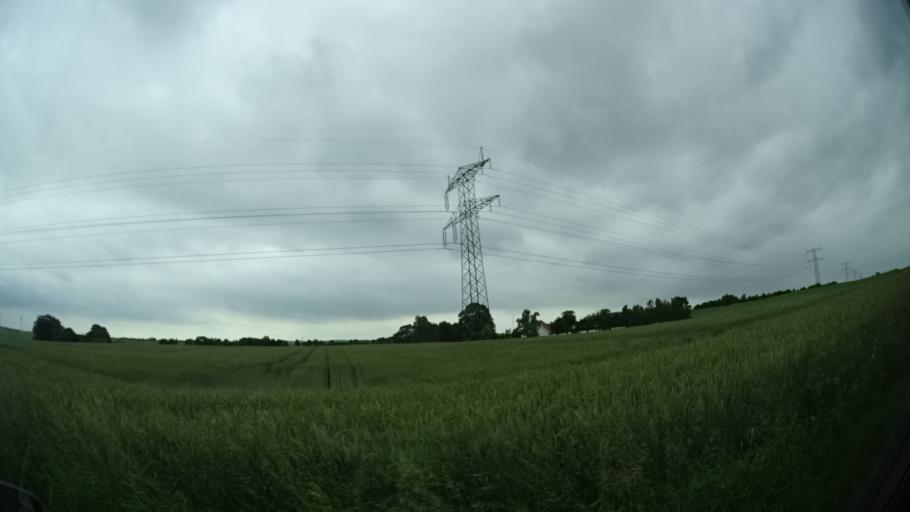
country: DK
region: Central Jutland
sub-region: Arhus Kommune
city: Kolt
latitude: 56.0819
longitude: 10.0833
